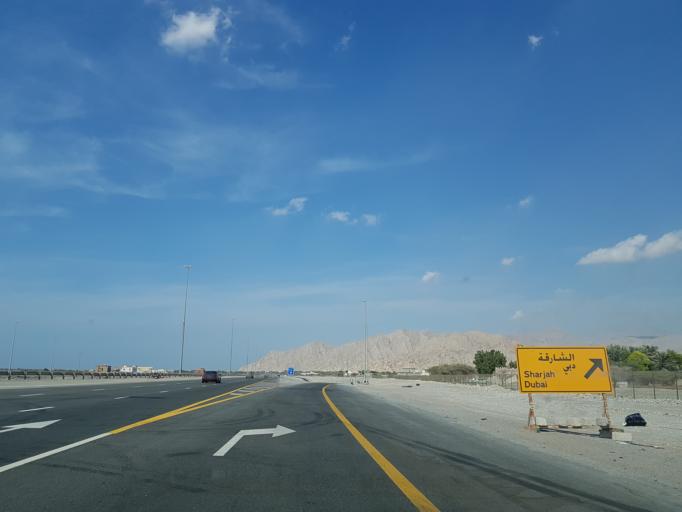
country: AE
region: Ra's al Khaymah
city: Ras al-Khaimah
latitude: 25.7941
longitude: 56.0312
